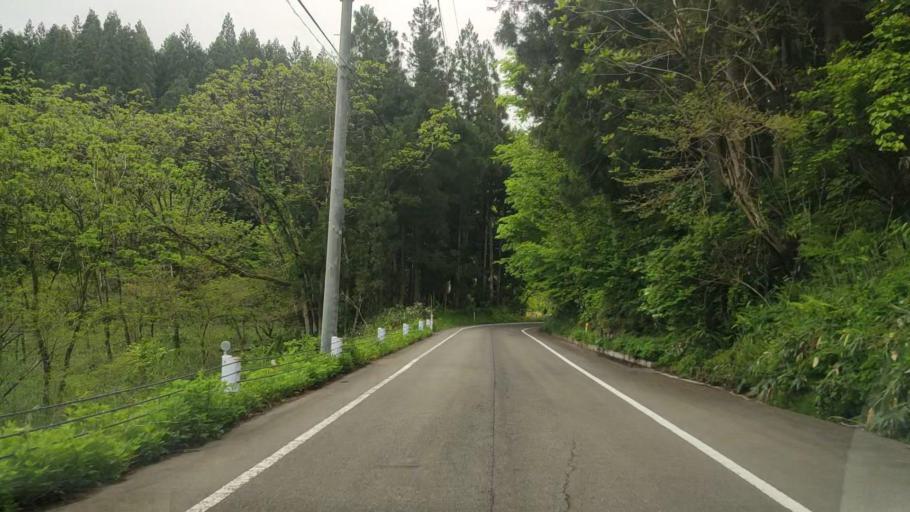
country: JP
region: Niigata
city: Gosen
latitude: 37.7140
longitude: 139.1230
